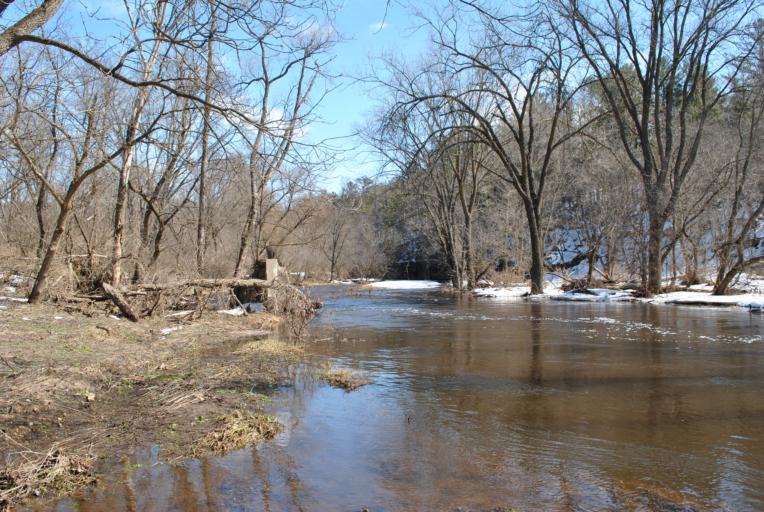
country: US
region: Wisconsin
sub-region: Pierce County
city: Spring Valley
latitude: 44.8675
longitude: -92.2518
